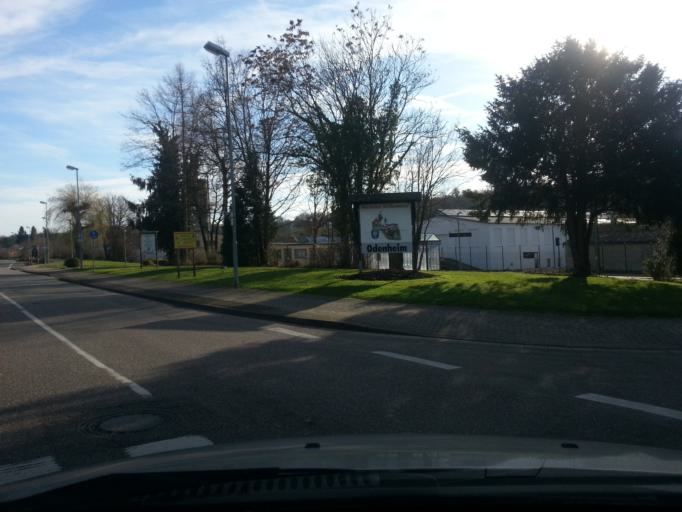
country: DE
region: Baden-Wuerttemberg
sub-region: Karlsruhe Region
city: Ostringen
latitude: 49.1827
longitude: 8.7363
